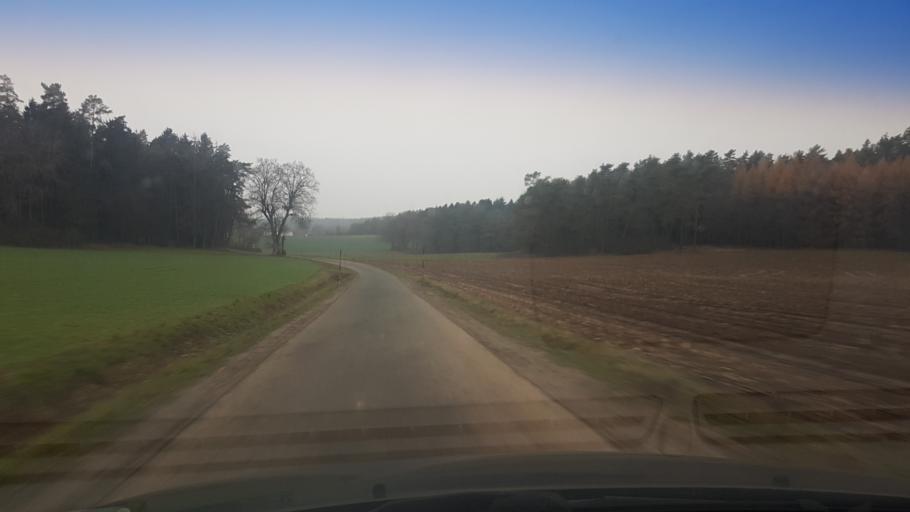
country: DE
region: Bavaria
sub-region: Upper Franconia
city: Wonsees
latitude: 50.0333
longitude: 11.2803
